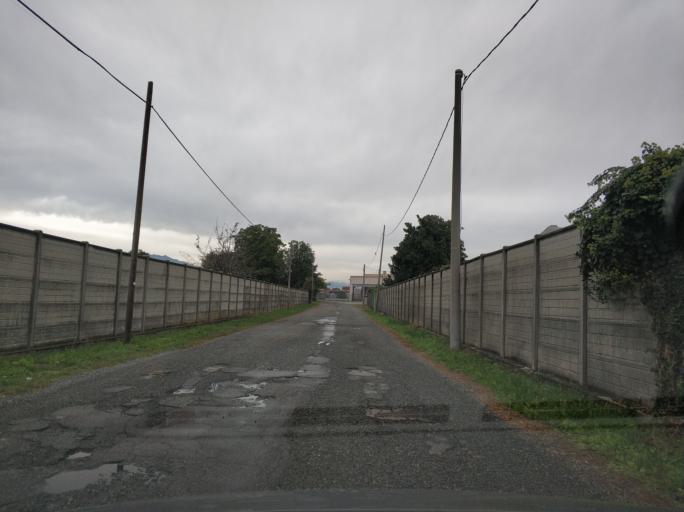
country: IT
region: Piedmont
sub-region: Provincia di Torino
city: Cirie
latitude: 45.2160
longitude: 7.6092
